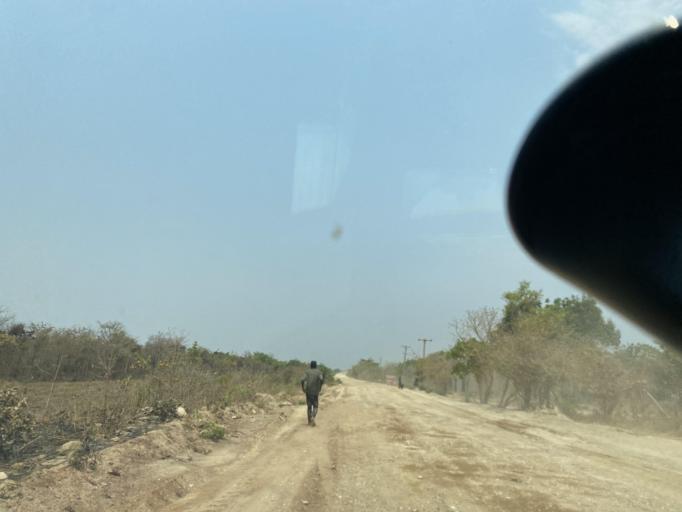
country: ZM
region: Lusaka
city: Lusaka
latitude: -15.5238
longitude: 28.3420
